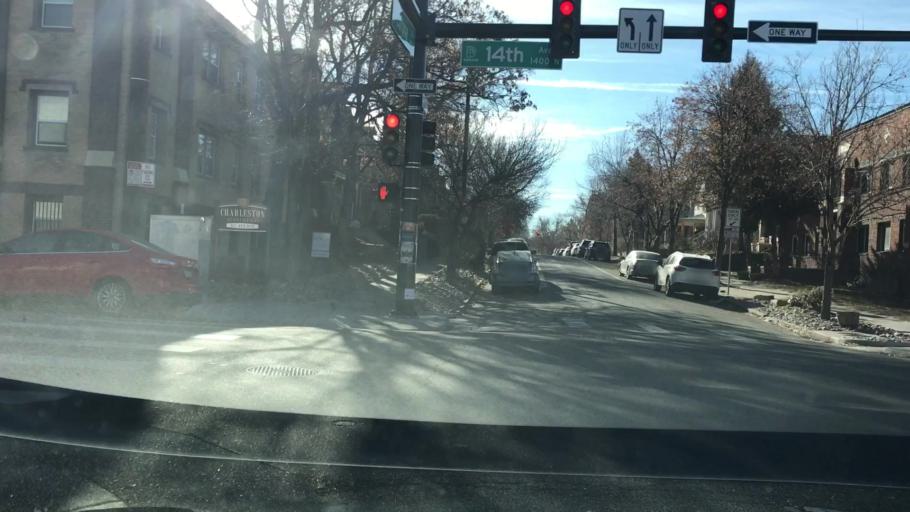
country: US
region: Colorado
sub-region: Denver County
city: Denver
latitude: 39.7385
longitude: -104.9741
